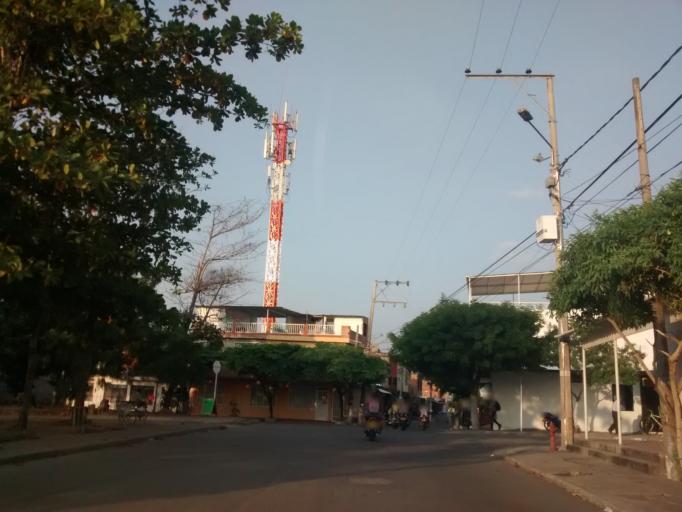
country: CO
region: Cundinamarca
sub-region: Girardot
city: Girardot City
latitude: 4.3154
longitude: -74.7862
